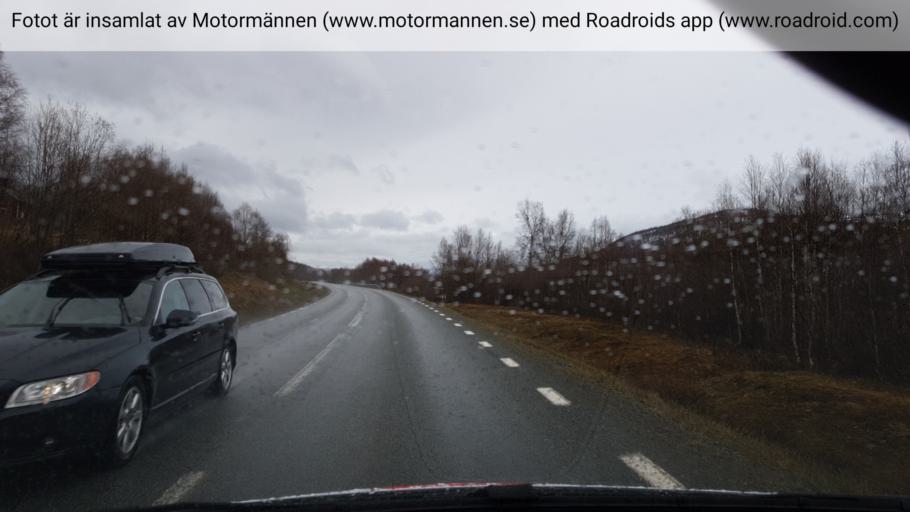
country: NO
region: Nordland
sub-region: Rana
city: Mo i Rana
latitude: 65.7942
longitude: 15.1005
